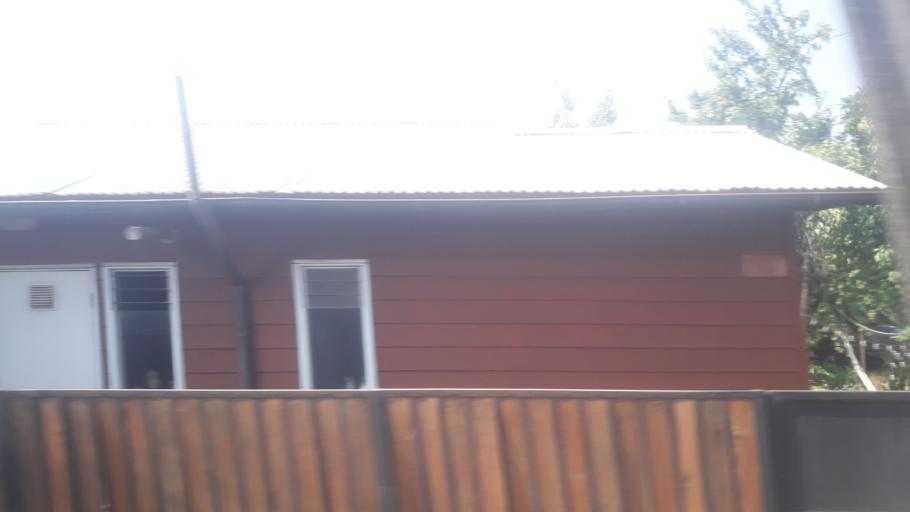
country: CL
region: Biobio
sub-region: Provincia de Concepcion
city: Lota
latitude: -37.1723
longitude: -72.9427
